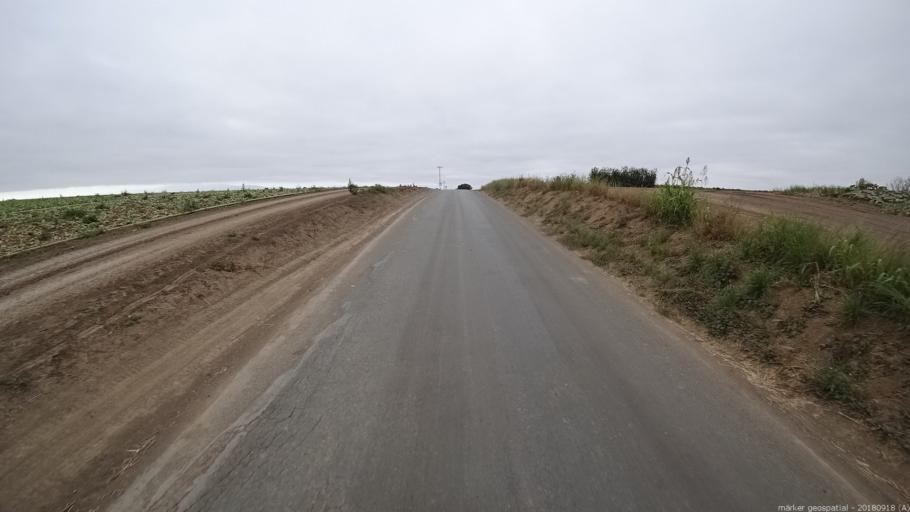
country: US
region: California
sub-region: Monterey County
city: Boronda
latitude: 36.7372
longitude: -121.6945
